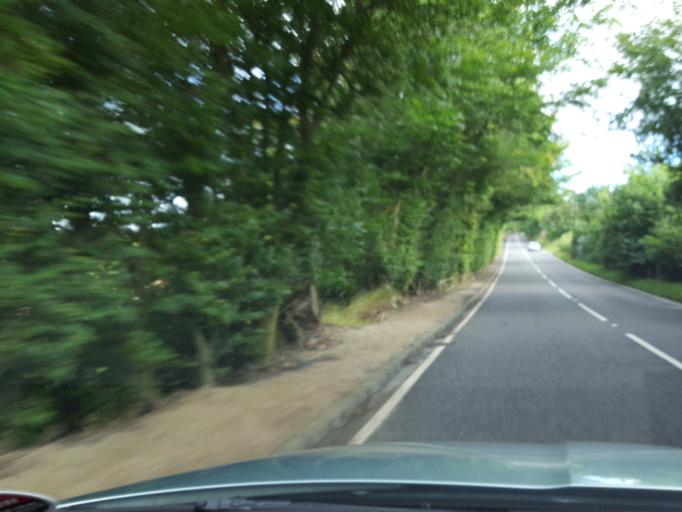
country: GB
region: Scotland
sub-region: West Lothian
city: Linlithgow
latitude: 55.9868
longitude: -3.6139
